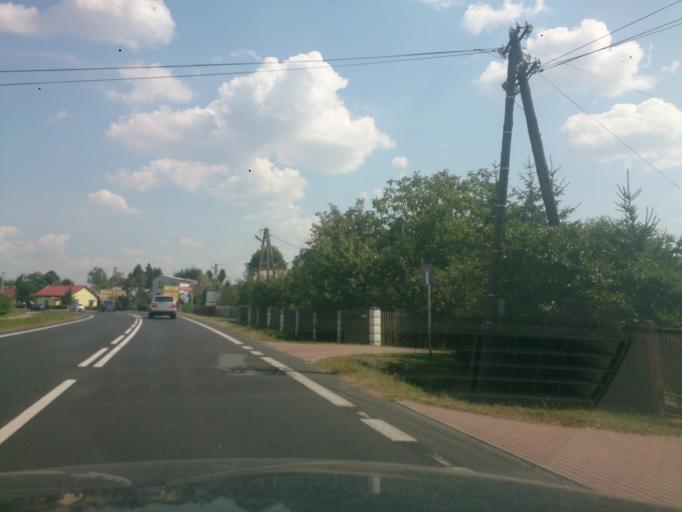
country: PL
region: Subcarpathian Voivodeship
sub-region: Powiat kolbuszowski
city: Majdan Krolewski
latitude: 50.3694
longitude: 21.7427
